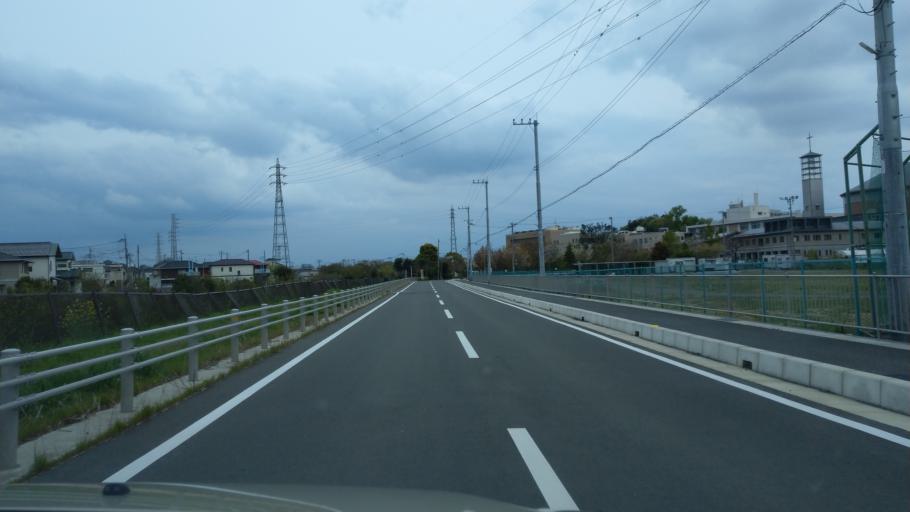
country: JP
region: Saitama
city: Ageoshimo
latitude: 35.9406
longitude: 139.5989
